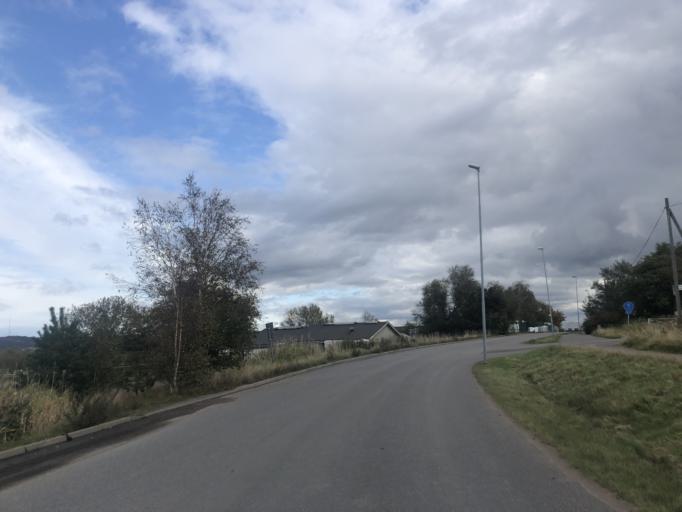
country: SE
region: Vaestra Goetaland
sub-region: Molndal
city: Moelndal
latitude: 57.6413
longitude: 11.9781
